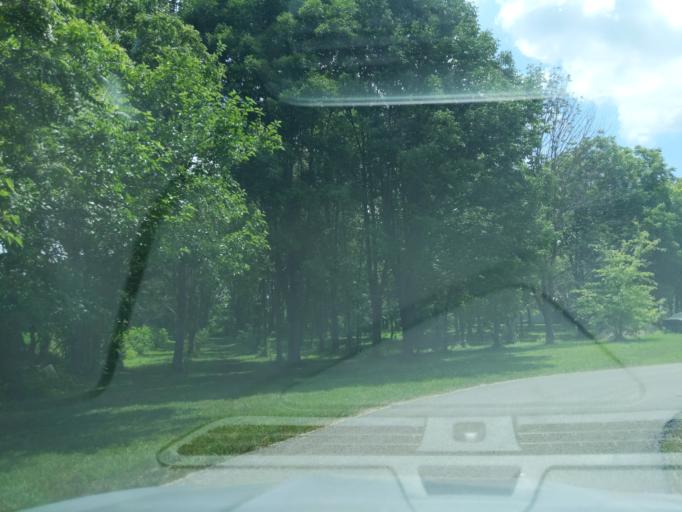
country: US
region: Indiana
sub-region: Ripley County
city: Osgood
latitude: 39.2062
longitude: -85.3230
